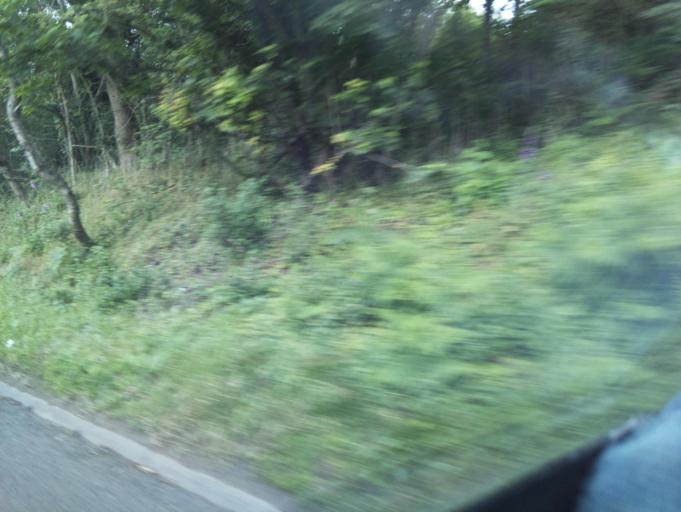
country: GB
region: England
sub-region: Worcestershire
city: Kidderminster
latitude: 52.4187
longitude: -2.2190
